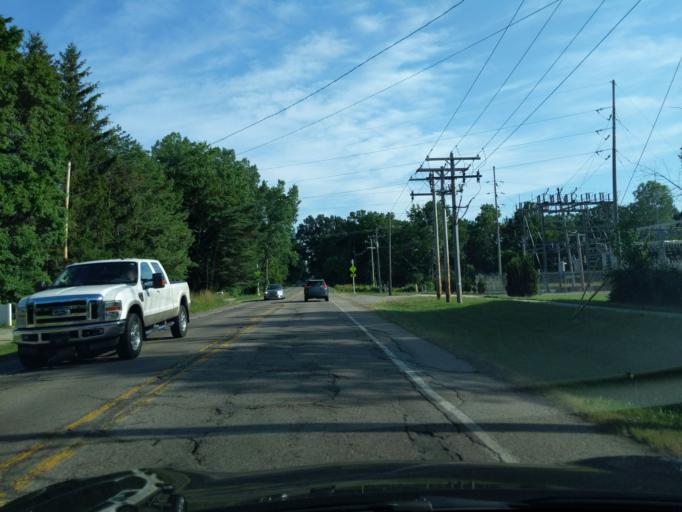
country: US
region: Michigan
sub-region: Ingham County
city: Okemos
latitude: 42.7416
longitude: -84.4277
